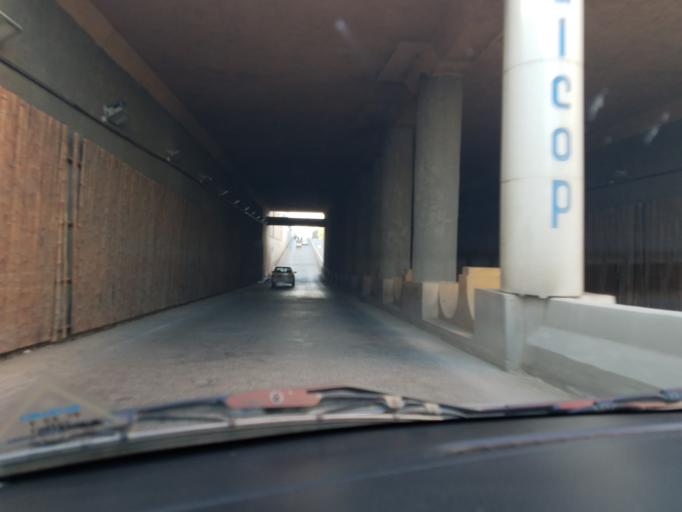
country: PK
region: Sindh
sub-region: Karachi District
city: Karachi
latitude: 24.8521
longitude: 67.0343
